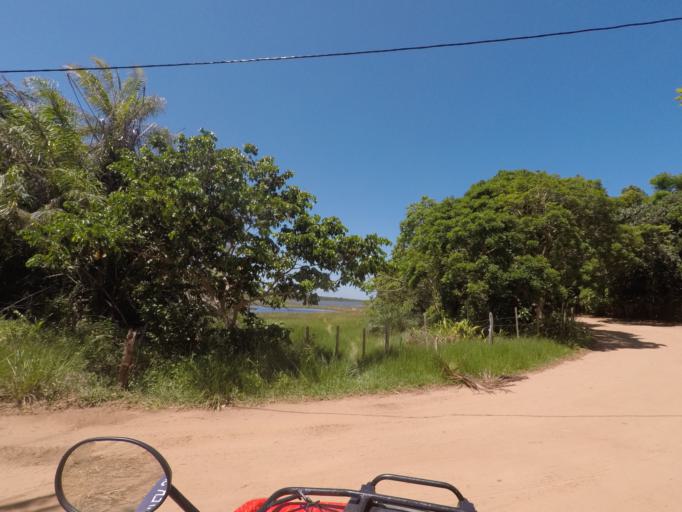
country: BR
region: Bahia
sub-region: Marau
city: Marau
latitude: -14.0254
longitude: -38.9500
